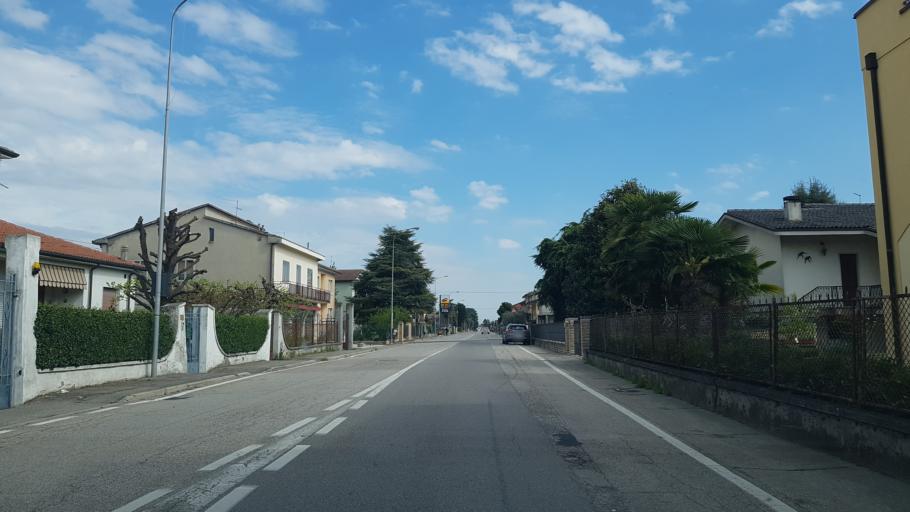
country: IT
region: Veneto
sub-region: Provincia di Verona
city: Belfiore
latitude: 45.3822
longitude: 11.2098
